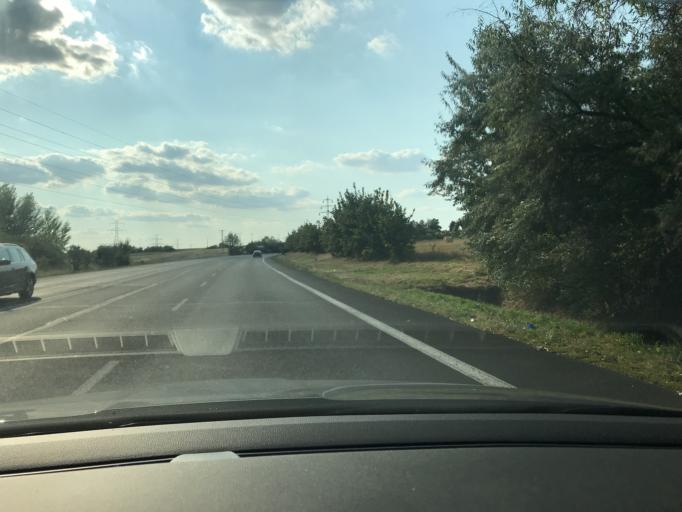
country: CZ
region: Ustecky
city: Peruc
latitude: 50.2906
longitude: 13.9234
